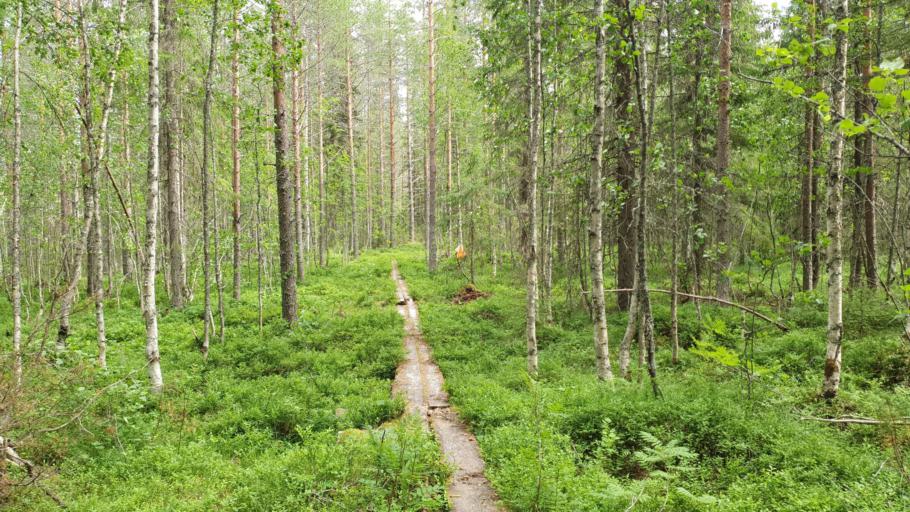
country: FI
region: Kainuu
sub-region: Kehys-Kainuu
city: Kuhmo
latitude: 63.9892
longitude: 29.4335
